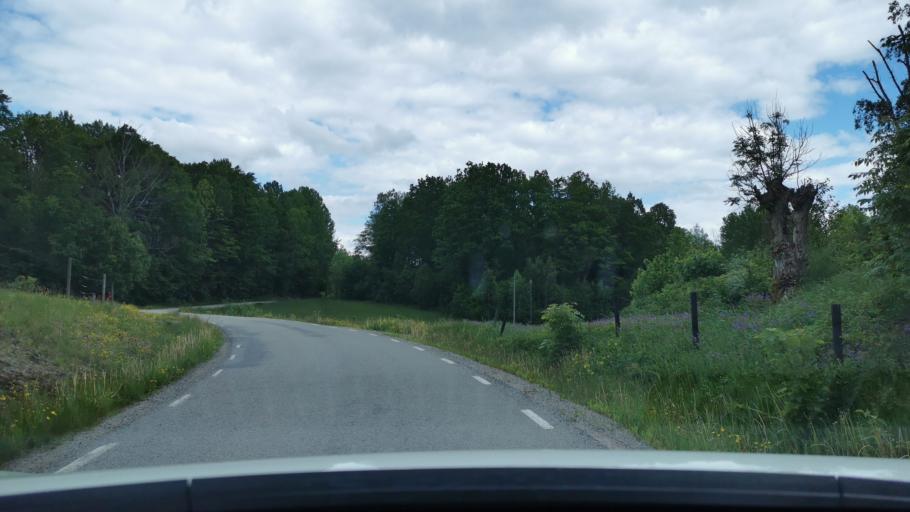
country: SE
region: Vaestra Goetaland
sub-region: Bengtsfors Kommun
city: Dals Langed
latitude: 58.8368
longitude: 12.3302
